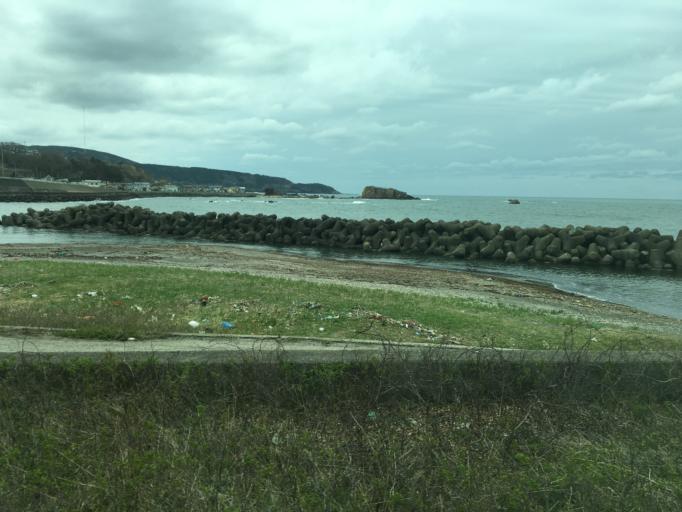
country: JP
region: Akita
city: Noshiromachi
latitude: 40.6566
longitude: 139.9378
